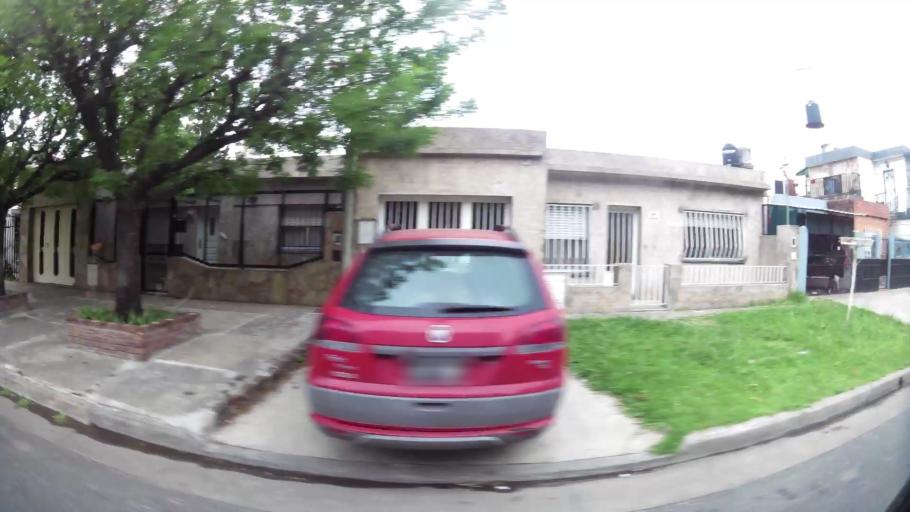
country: AR
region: Santa Fe
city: Gobernador Galvez
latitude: -32.9936
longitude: -60.6671
